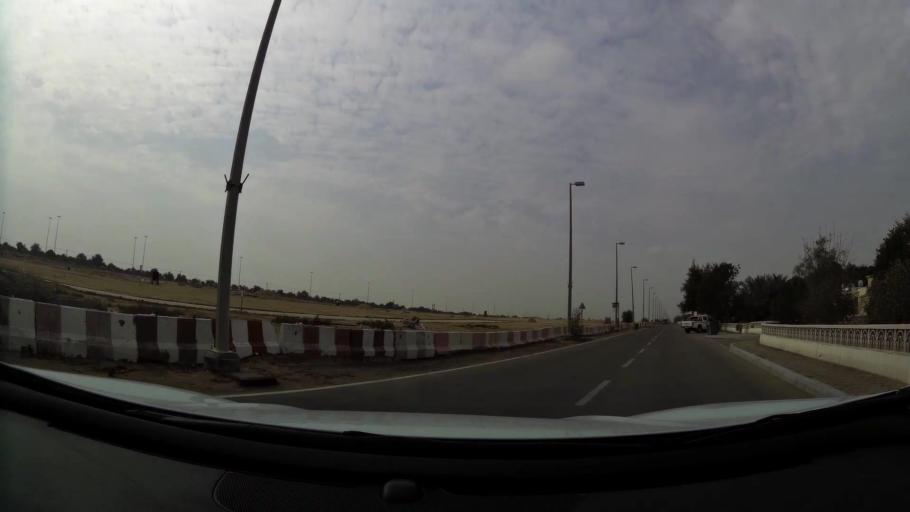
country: AE
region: Abu Dhabi
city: Abu Dhabi
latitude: 24.6518
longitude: 54.7406
